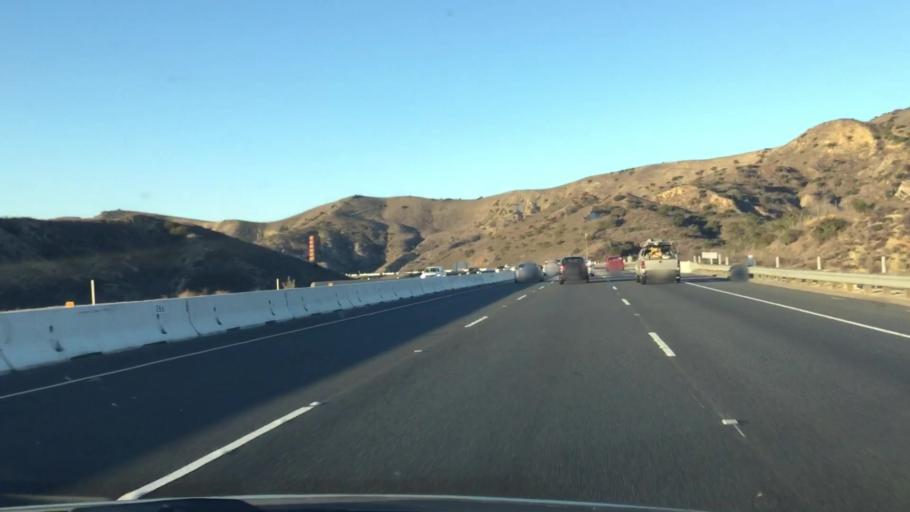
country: US
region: California
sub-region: Orange County
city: Foothill Ranch
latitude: 33.7362
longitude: -117.7177
